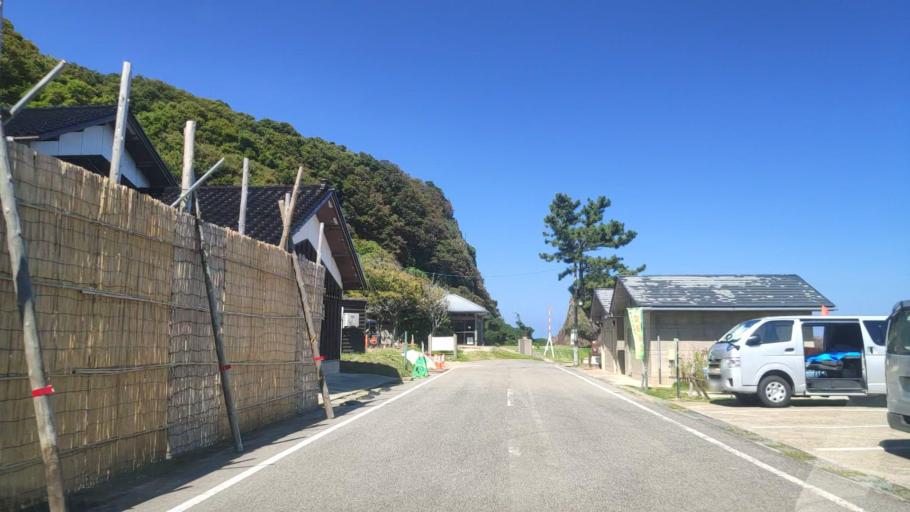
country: JP
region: Ishikawa
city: Nanao
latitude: 37.5285
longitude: 137.2646
